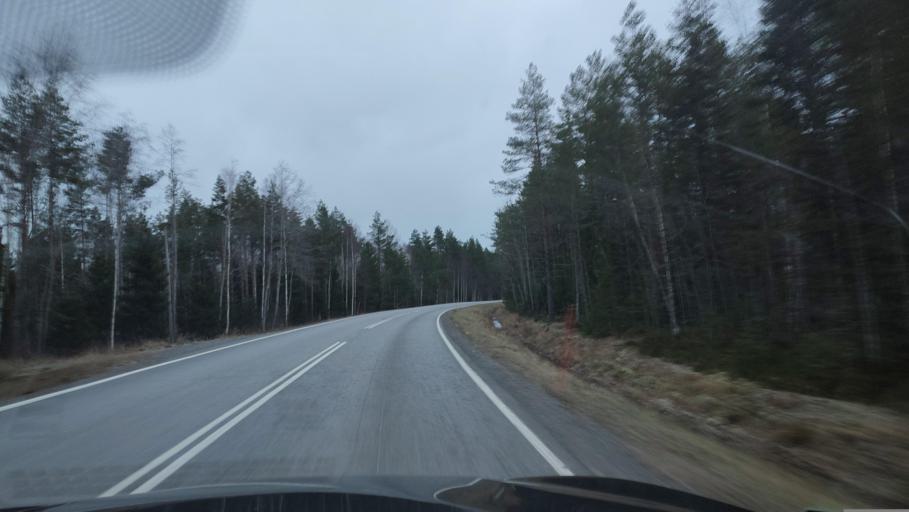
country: FI
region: Southern Ostrobothnia
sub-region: Suupohja
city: Karijoki
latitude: 62.3307
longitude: 21.9020
